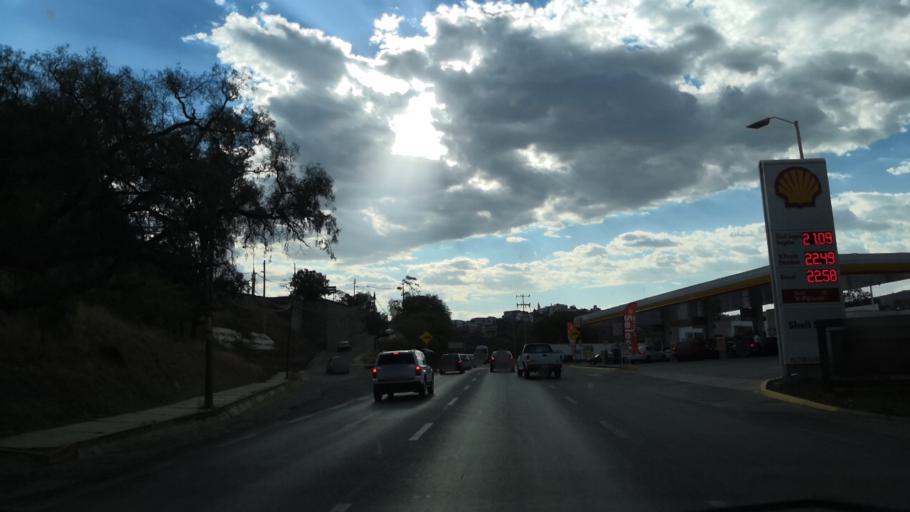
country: MX
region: Guanajuato
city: Guanajuato
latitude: 21.0096
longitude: -101.2696
